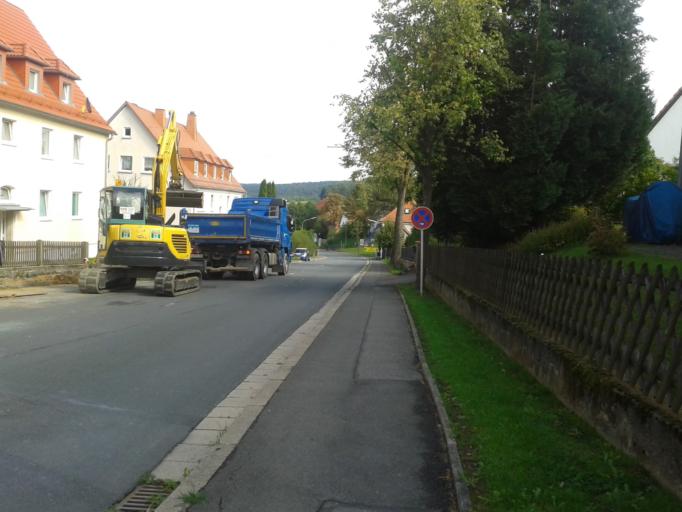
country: DE
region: Bavaria
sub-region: Upper Franconia
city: Marktschorgast
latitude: 50.0917
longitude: 11.6532
